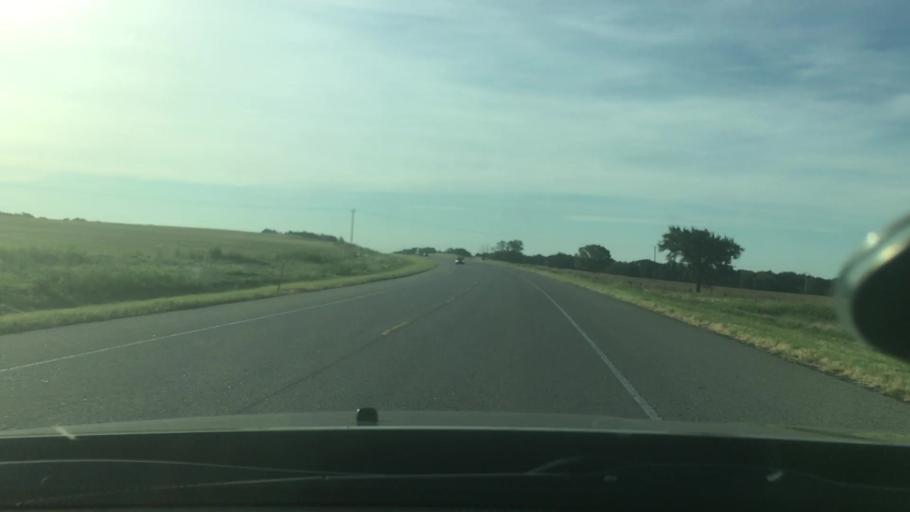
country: US
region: Oklahoma
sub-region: Pontotoc County
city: Ada
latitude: 34.6851
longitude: -96.5913
